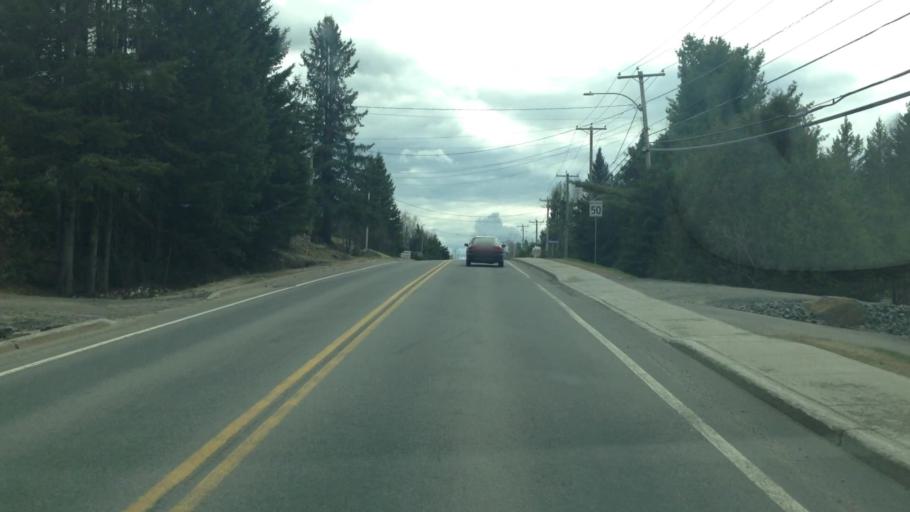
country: CA
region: Quebec
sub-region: Laurentides
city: Sainte-Adele
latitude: 46.0273
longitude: -74.0647
